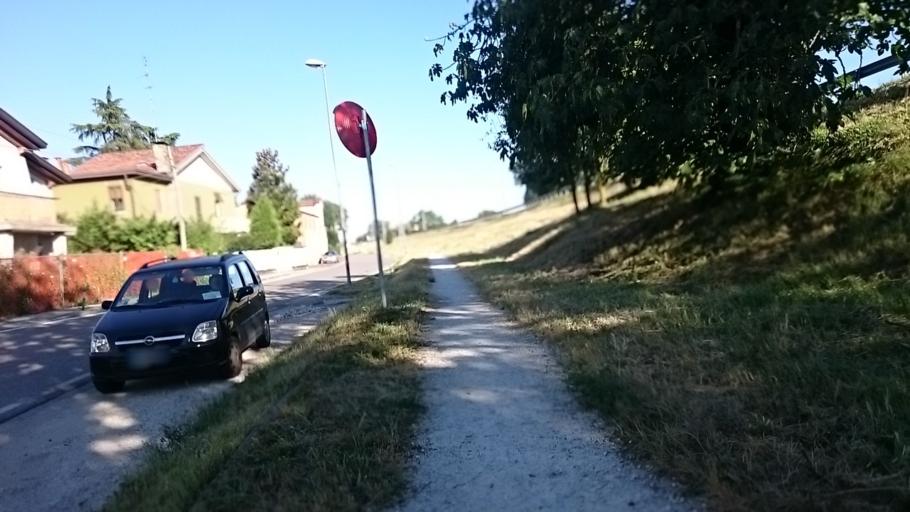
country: IT
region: Veneto
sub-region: Provincia di Padova
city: Mejaniga
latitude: 45.4451
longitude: 11.8977
